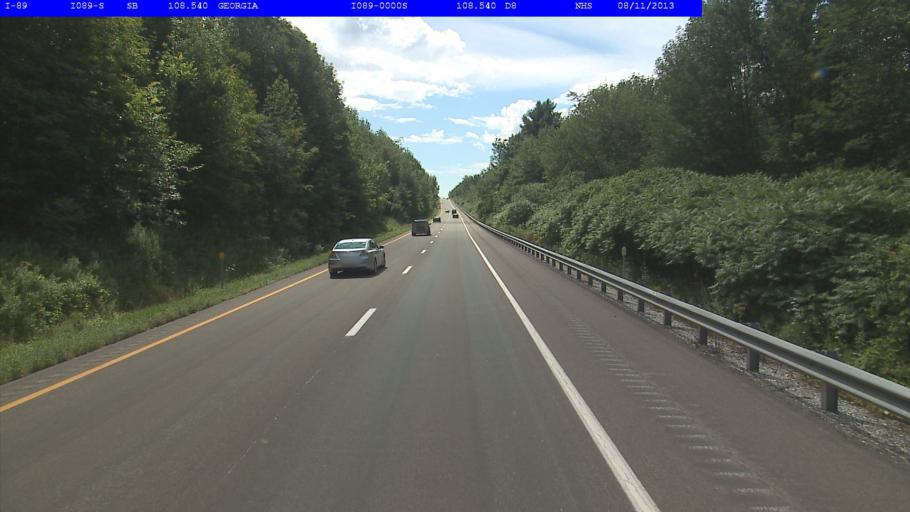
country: US
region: Vermont
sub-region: Chittenden County
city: Milton
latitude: 44.7206
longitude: -73.0842
